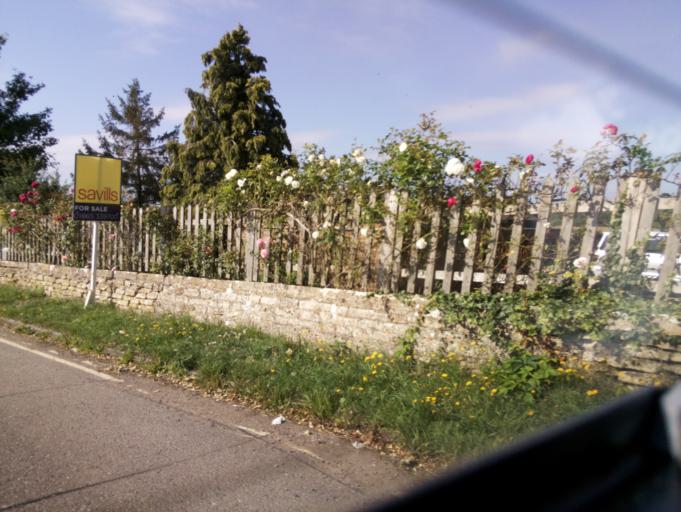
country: GB
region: England
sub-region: Oxfordshire
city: Faringdon
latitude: 51.6932
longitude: -1.5885
